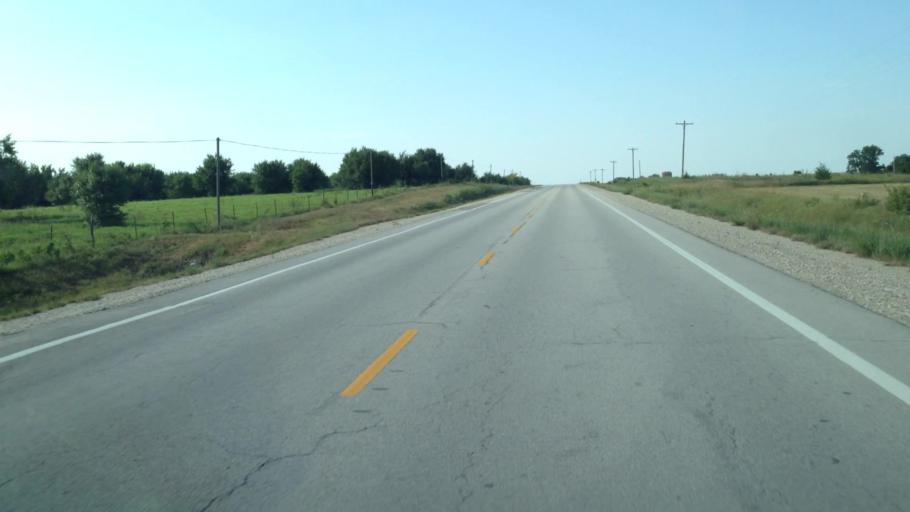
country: US
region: Kansas
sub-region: Anderson County
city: Garnett
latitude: 38.1113
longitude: -95.2427
